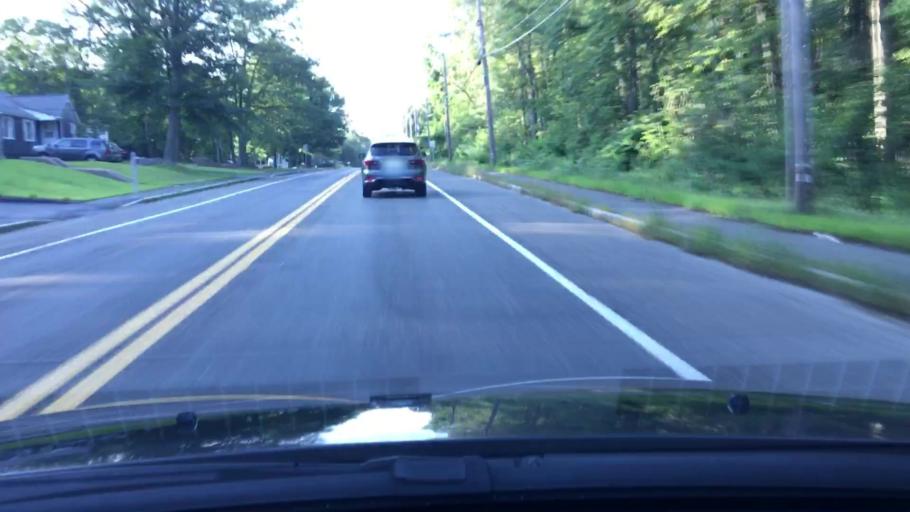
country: US
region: Massachusetts
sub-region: Worcester County
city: Shrewsbury
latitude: 42.3041
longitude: -71.7162
